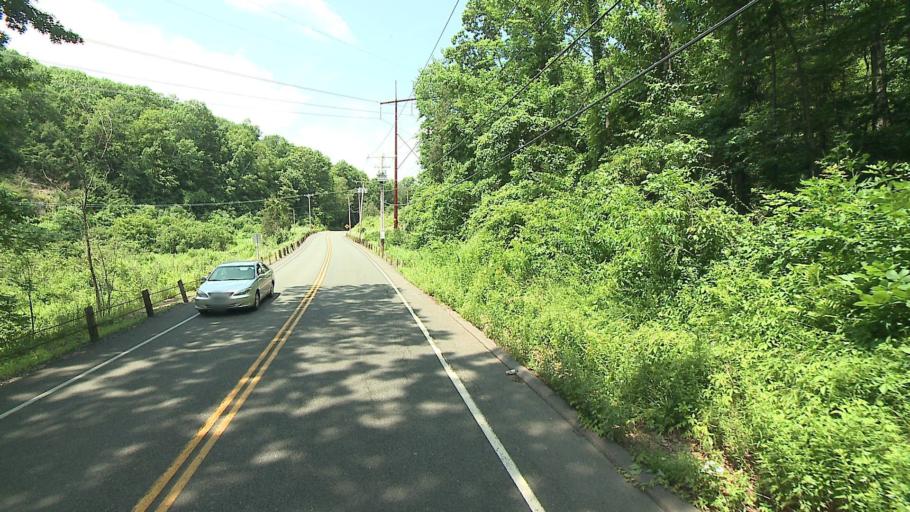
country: US
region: Connecticut
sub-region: Hartford County
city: Tariffville
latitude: 41.9211
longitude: -72.7494
